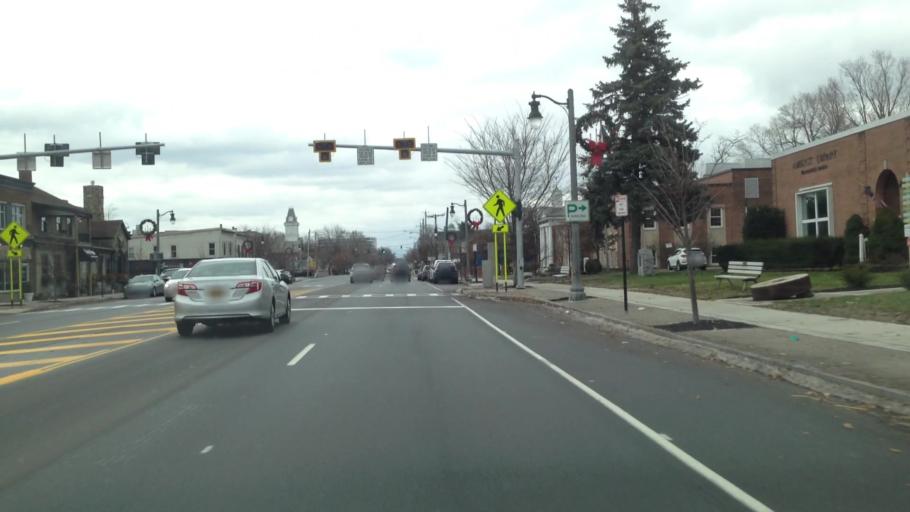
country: US
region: New York
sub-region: Erie County
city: Williamsville
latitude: 42.9626
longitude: -78.7459
